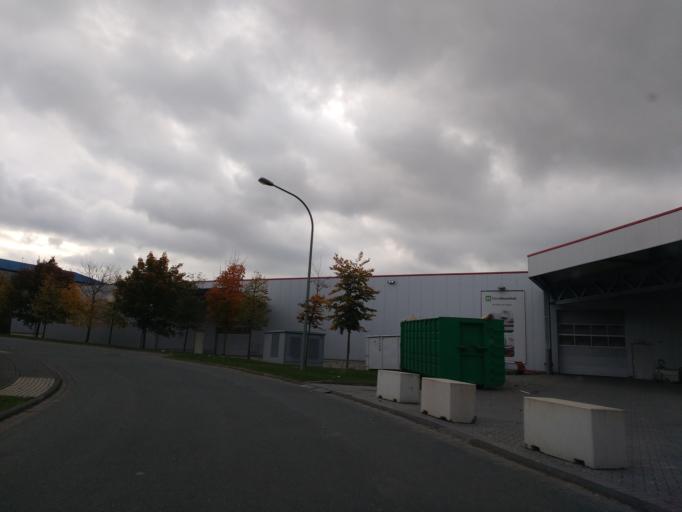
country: DE
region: North Rhine-Westphalia
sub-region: Regierungsbezirk Detmold
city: Paderborn
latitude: 51.6463
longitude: 8.7127
